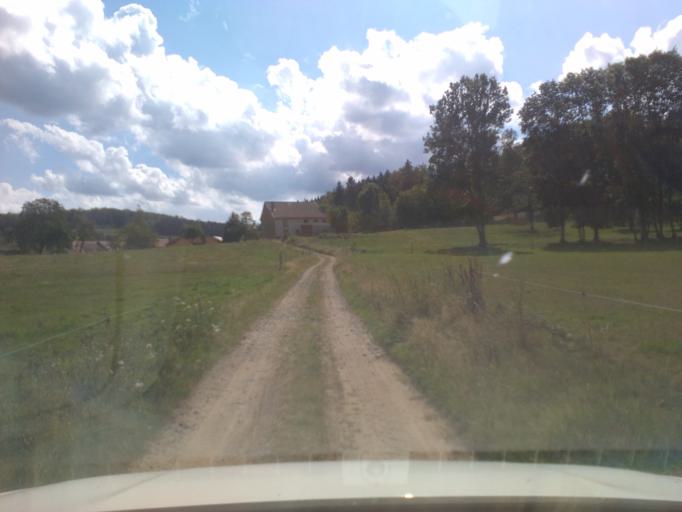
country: FR
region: Lorraine
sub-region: Departement des Vosges
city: Senones
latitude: 48.3822
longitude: 7.0197
